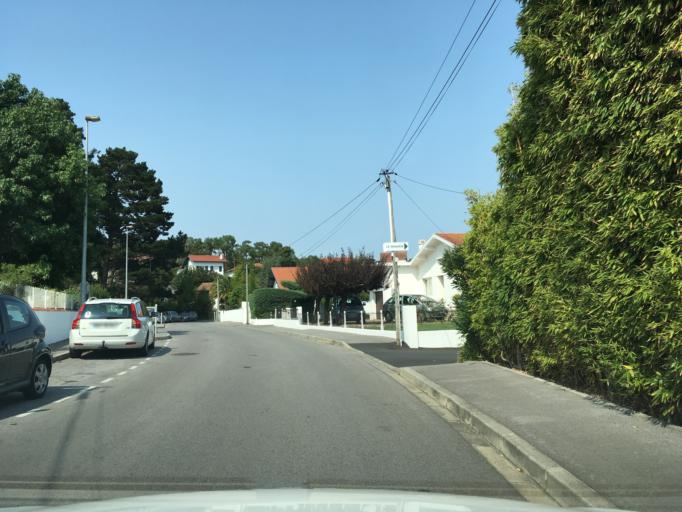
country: FR
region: Aquitaine
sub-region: Departement des Pyrenees-Atlantiques
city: Anglet
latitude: 43.5005
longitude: -1.5159
